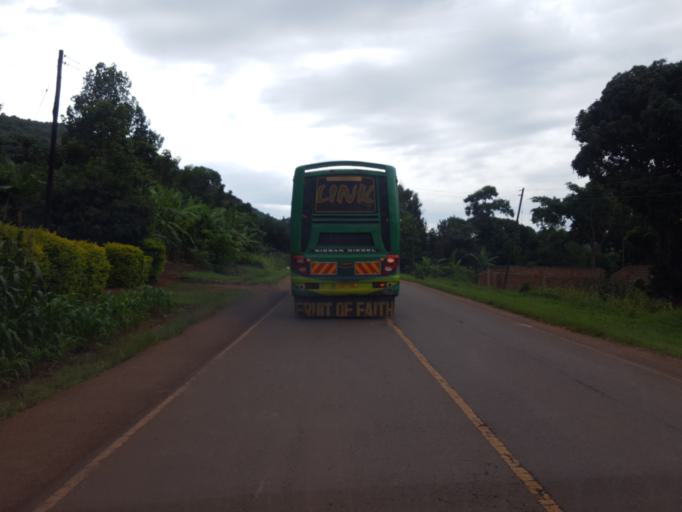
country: UG
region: Central Region
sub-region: Mityana District
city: Mityana
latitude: 0.6719
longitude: 32.0790
